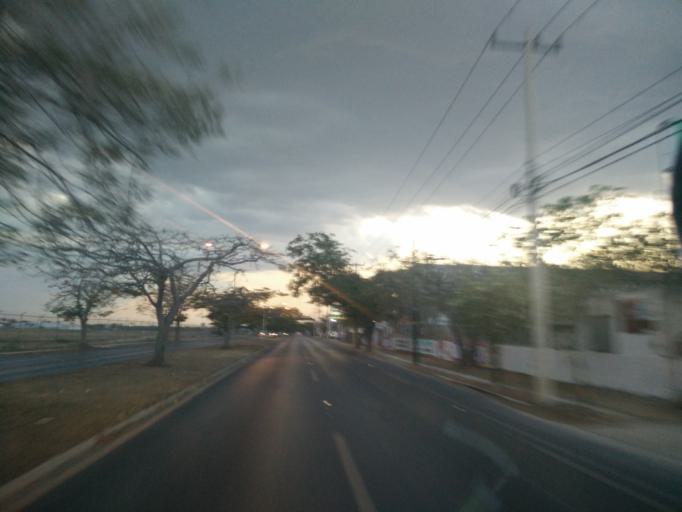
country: MX
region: Yucatan
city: Itzincab Palomeque
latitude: 20.9440
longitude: -89.6575
